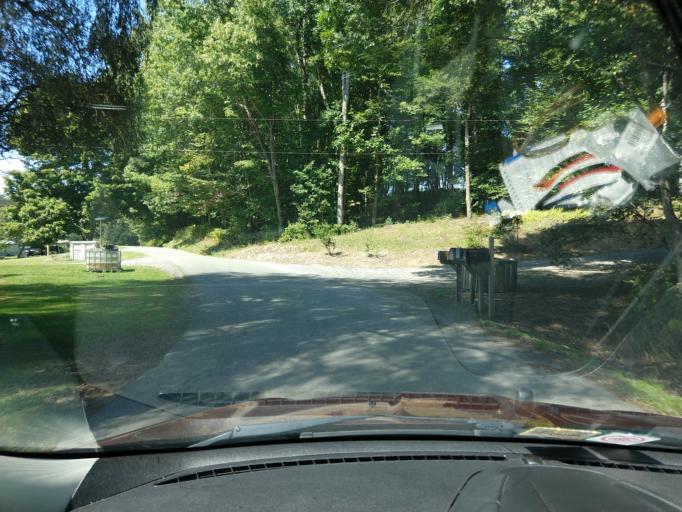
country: US
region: West Virginia
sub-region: Nicholas County
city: Craigsville
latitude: 38.2823
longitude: -80.7357
